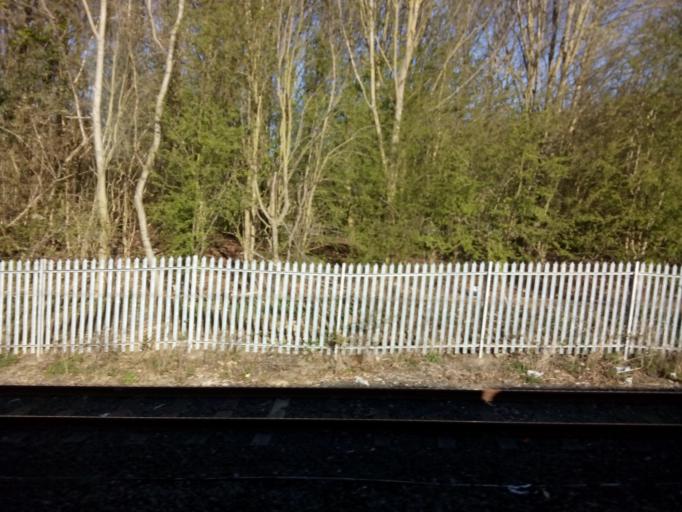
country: GB
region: England
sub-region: County Durham
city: Durham
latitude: 54.7830
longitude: -1.5786
